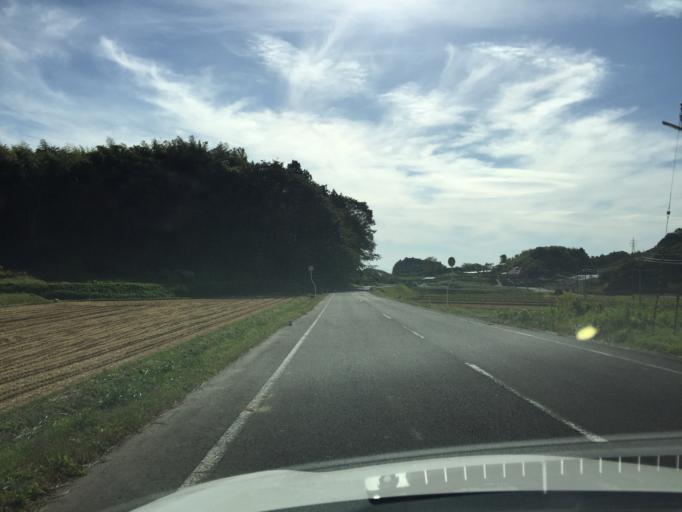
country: JP
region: Fukushima
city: Miharu
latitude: 37.4795
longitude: 140.4949
